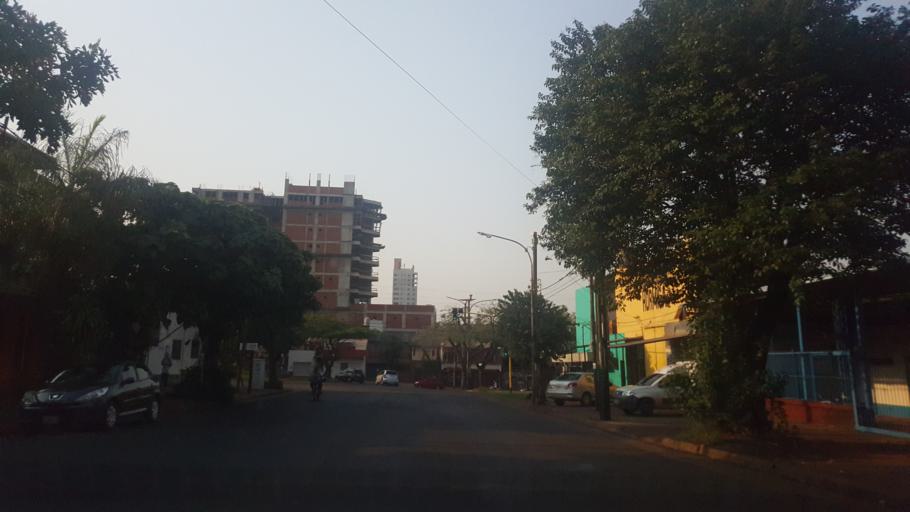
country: AR
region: Misiones
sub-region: Departamento de Capital
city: Posadas
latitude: -27.3758
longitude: -55.8911
